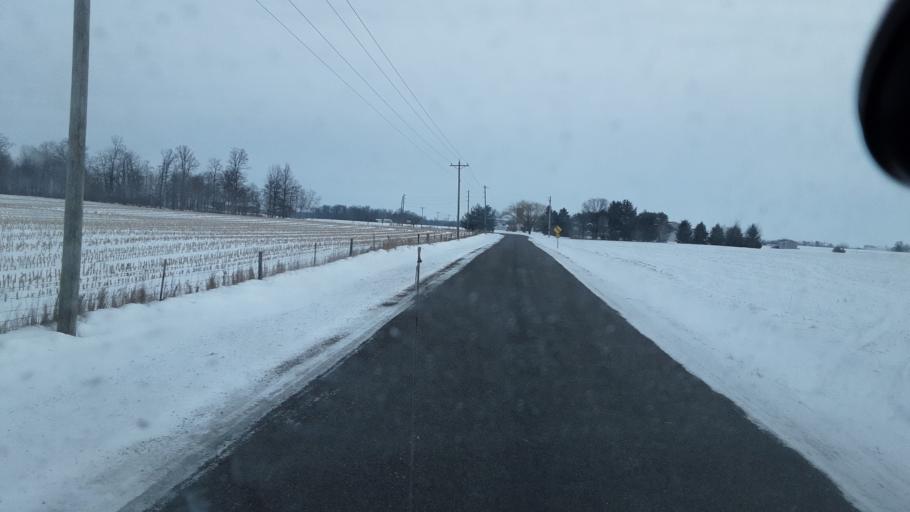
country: US
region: Ohio
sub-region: Union County
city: Marysville
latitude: 40.1638
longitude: -83.3643
